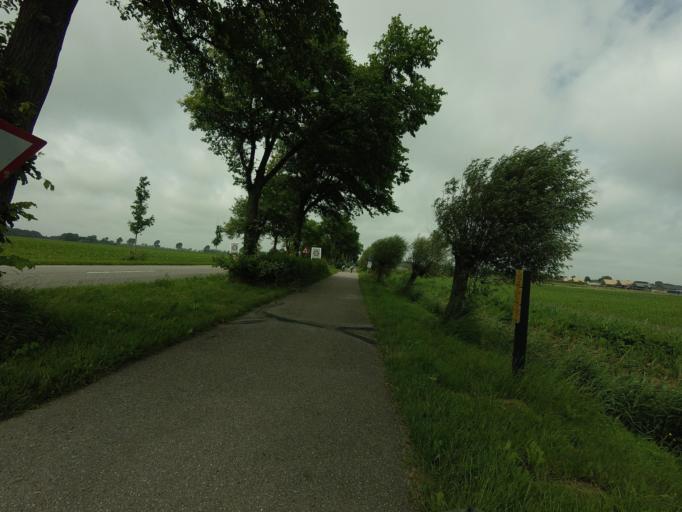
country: NL
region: North Holland
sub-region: Gemeente Schagen
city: Harenkarspel
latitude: 52.7323
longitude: 4.7378
